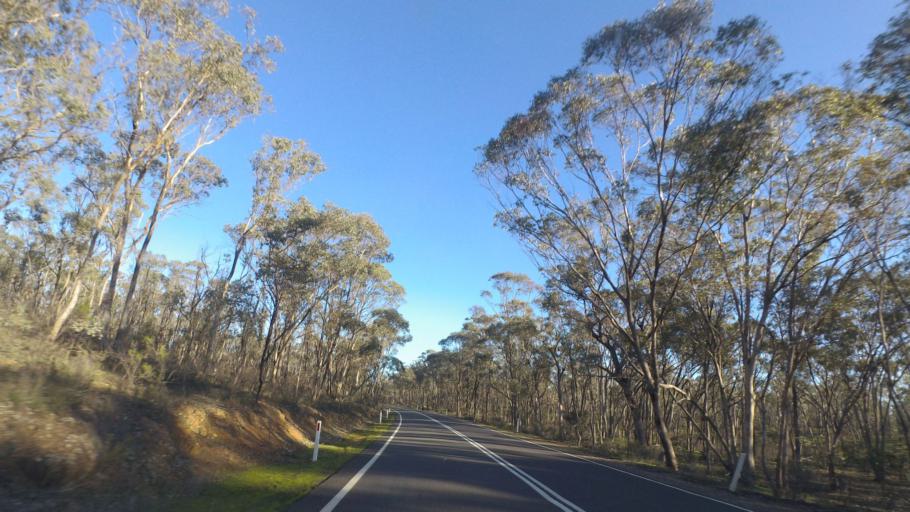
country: AU
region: Victoria
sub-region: Greater Bendigo
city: Kennington
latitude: -36.9176
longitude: 144.4917
